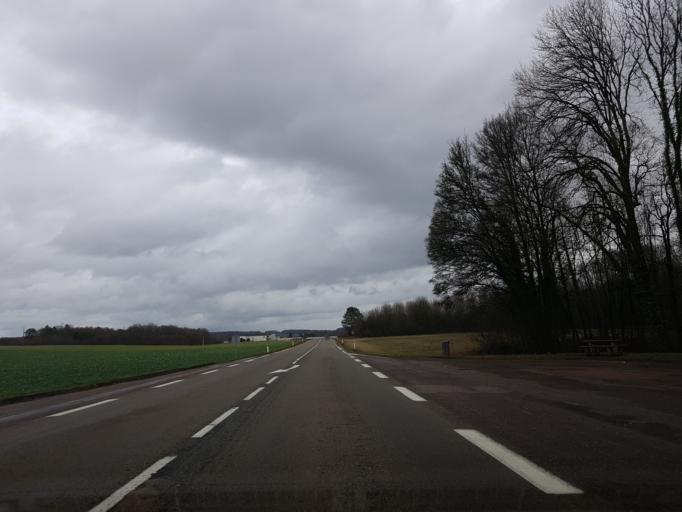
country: FR
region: Franche-Comte
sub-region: Departement de la Haute-Saone
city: Jussey
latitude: 47.7180
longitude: 5.8735
